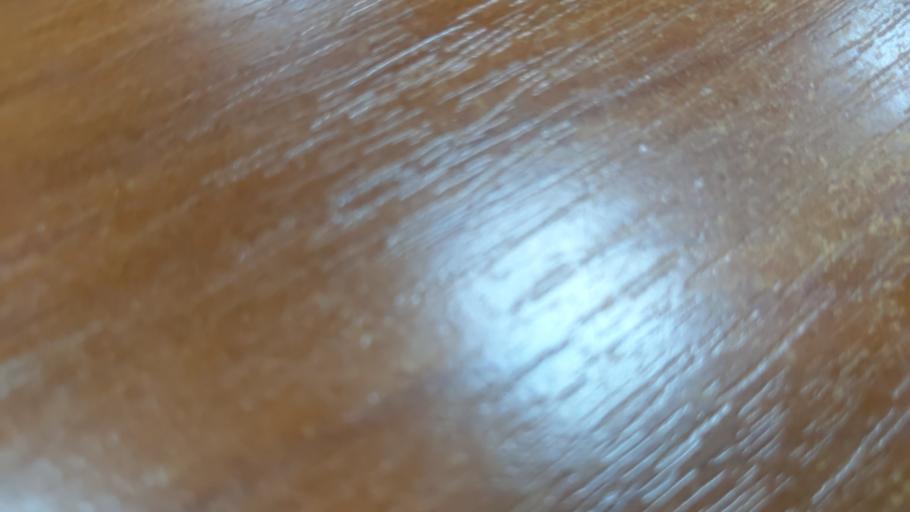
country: RU
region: Moskovskaya
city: Aprelevka
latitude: 55.5342
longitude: 37.0603
